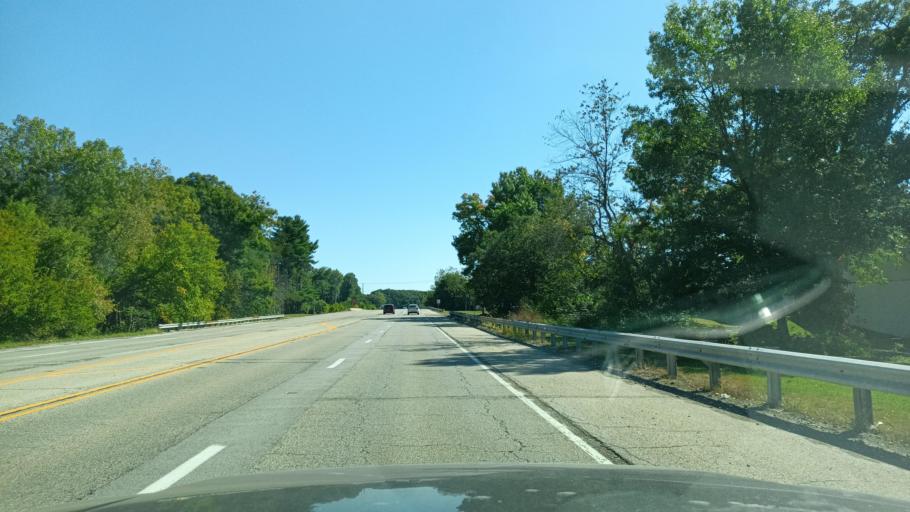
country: US
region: Illinois
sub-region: Peoria County
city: West Peoria
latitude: 40.7699
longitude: -89.6523
